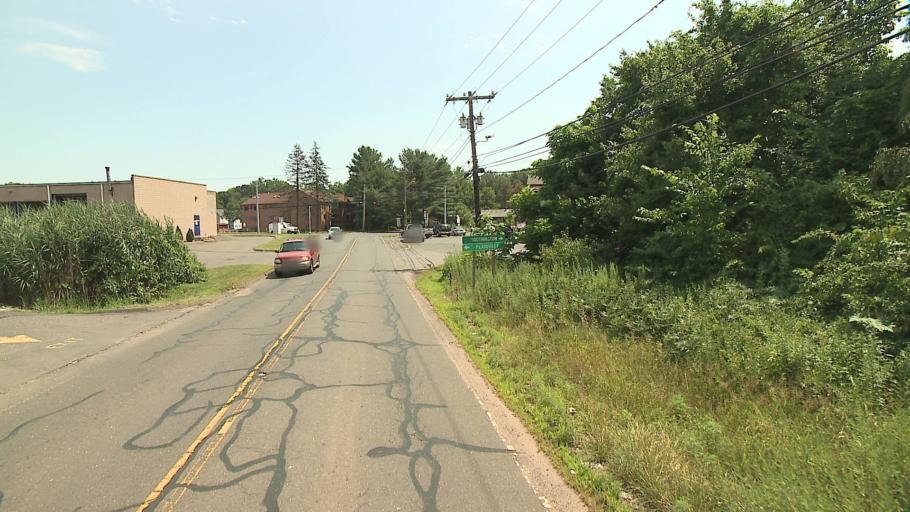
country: US
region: Connecticut
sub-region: Hartford County
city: Plainville
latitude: 41.6509
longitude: -72.8715
